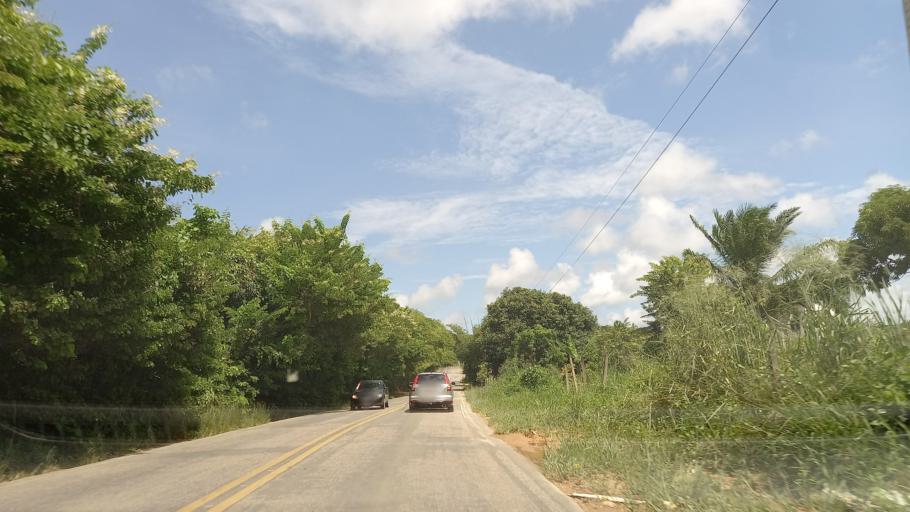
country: BR
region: Pernambuco
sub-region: Barreiros
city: Barreiros
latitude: -8.8269
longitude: -35.1767
